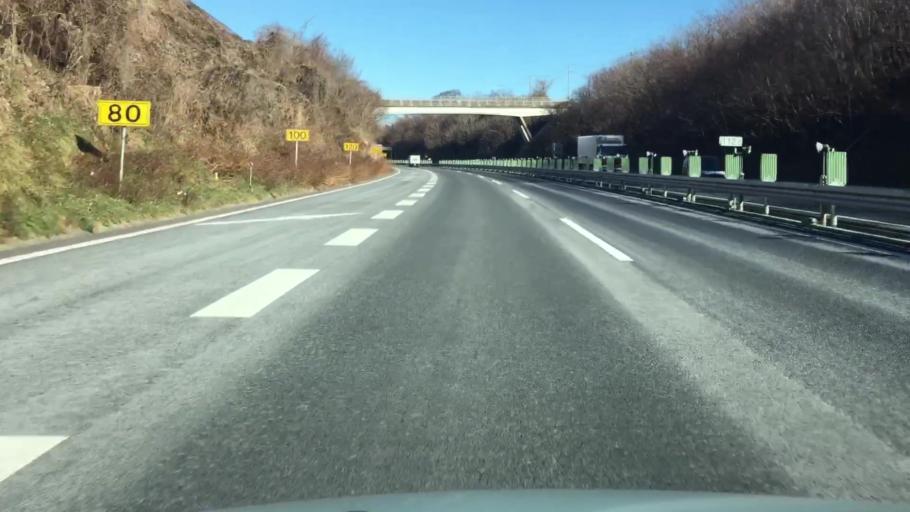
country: JP
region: Gunma
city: Shibukawa
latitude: 36.5437
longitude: 139.0516
